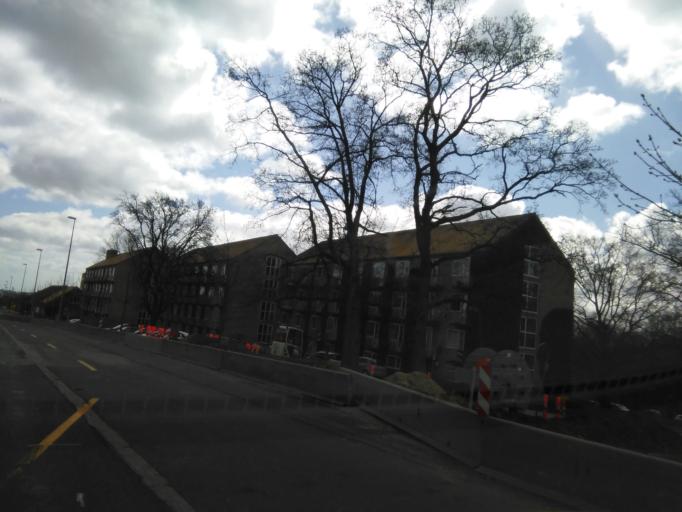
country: DK
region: Central Jutland
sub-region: Arhus Kommune
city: Arhus
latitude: 56.1700
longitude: 10.2055
